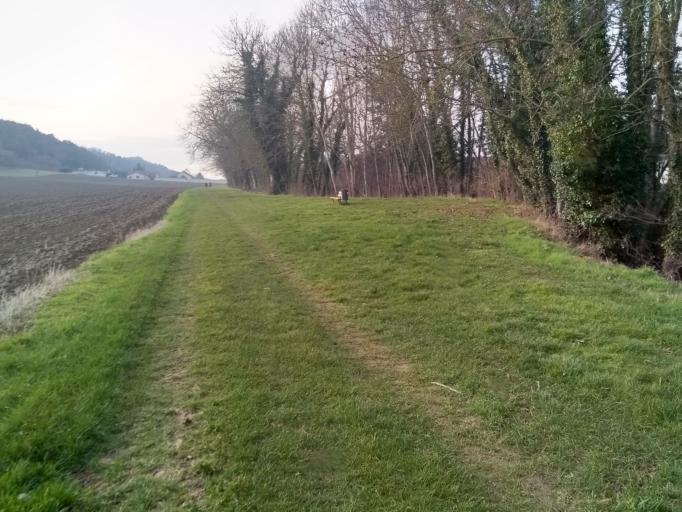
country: FR
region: Bourgogne
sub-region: Departement de l'Yonne
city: Malay-le-Grand
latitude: 48.1693
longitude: 3.3430
